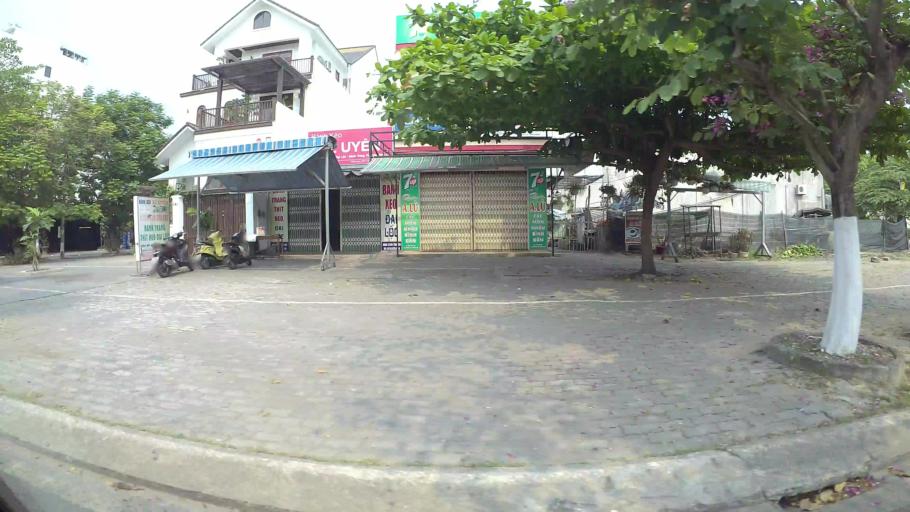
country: VN
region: Da Nang
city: Son Tra
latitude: 16.0409
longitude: 108.2179
